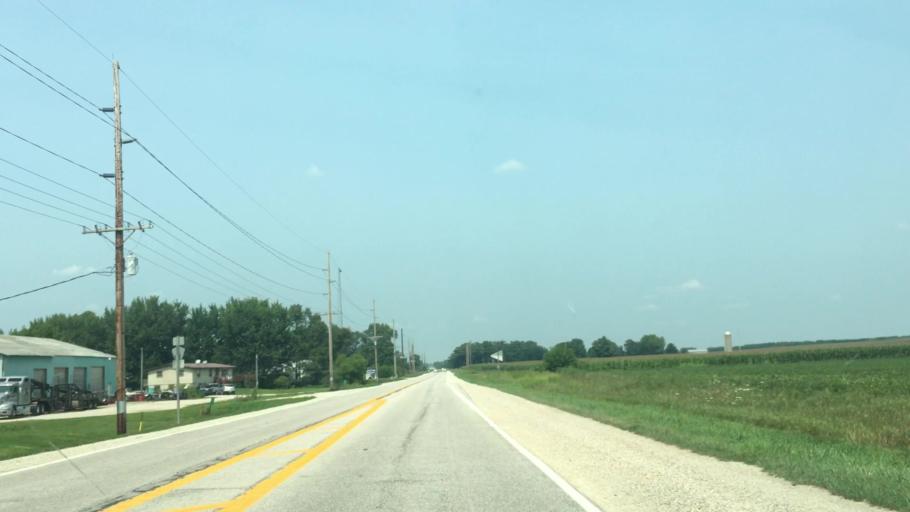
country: US
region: Iowa
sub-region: Buchanan County
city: Independence
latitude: 42.3732
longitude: -91.8893
